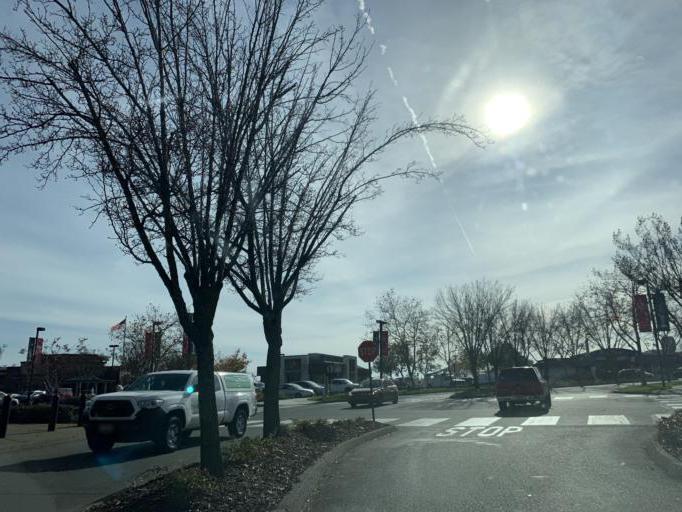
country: US
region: California
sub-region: El Dorado County
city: El Dorado Hills
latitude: 38.6551
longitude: -121.0698
